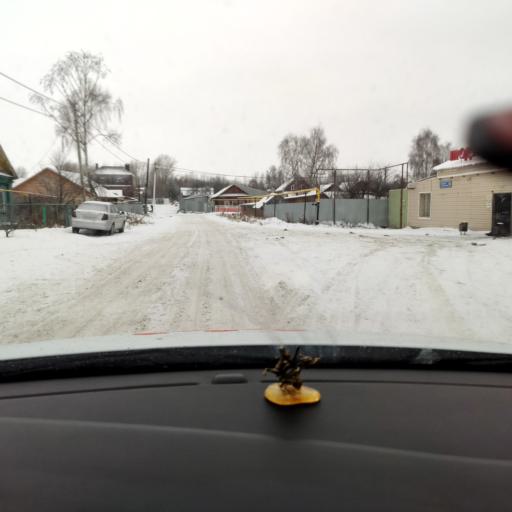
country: RU
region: Tatarstan
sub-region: Gorod Kazan'
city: Kazan
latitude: 55.7392
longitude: 49.0974
